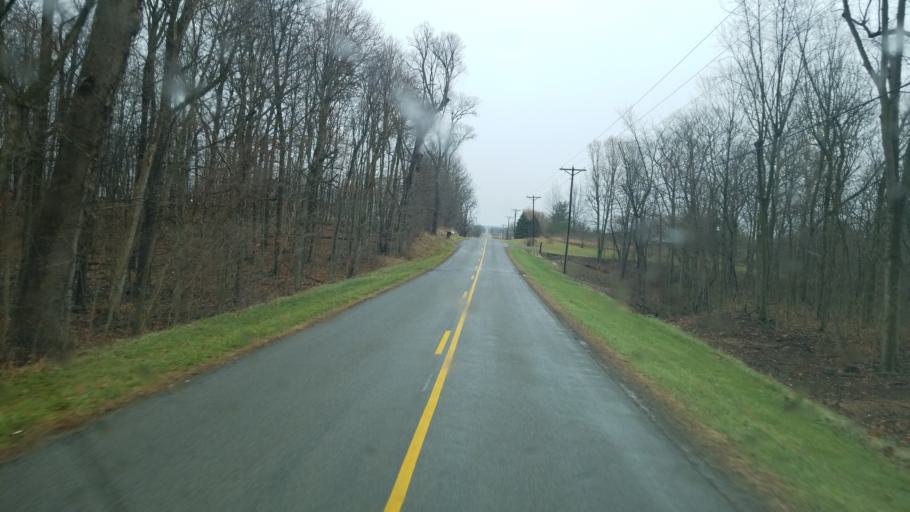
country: US
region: Ohio
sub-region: Logan County
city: Northwood
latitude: 40.4450
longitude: -83.6449
